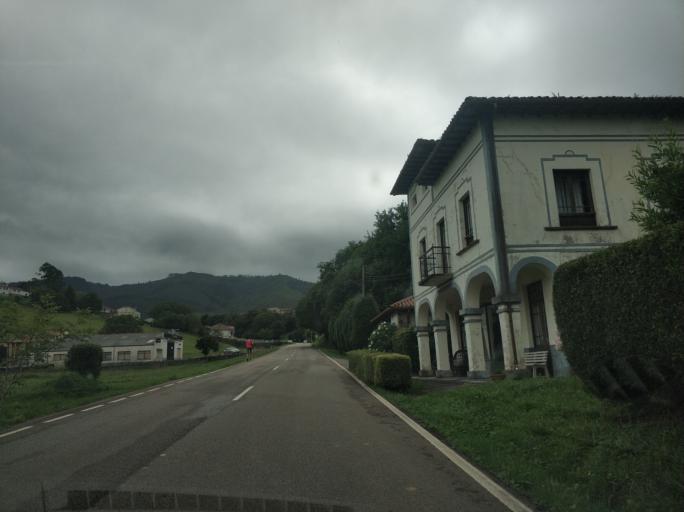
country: ES
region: Asturias
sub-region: Province of Asturias
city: Cudillero
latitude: 43.5490
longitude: -6.2233
